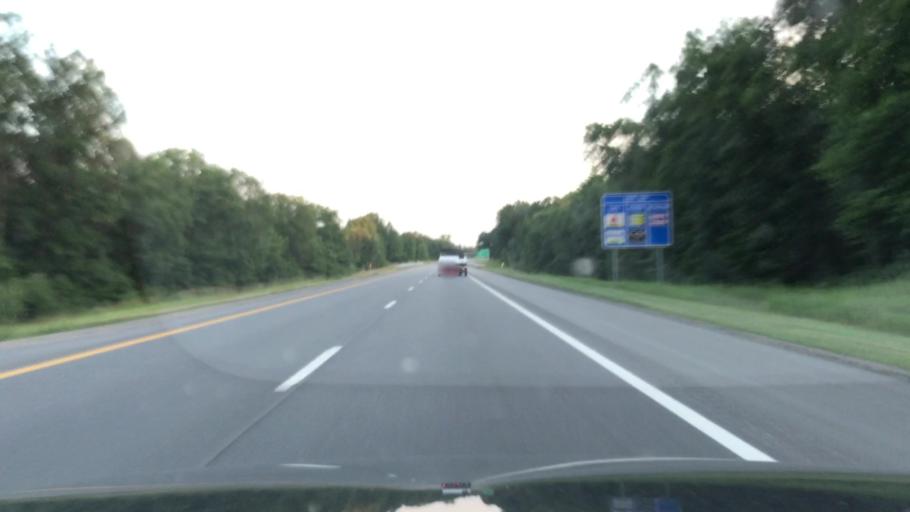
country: US
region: Michigan
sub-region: Montcalm County
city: Howard City
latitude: 43.4356
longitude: -85.4938
